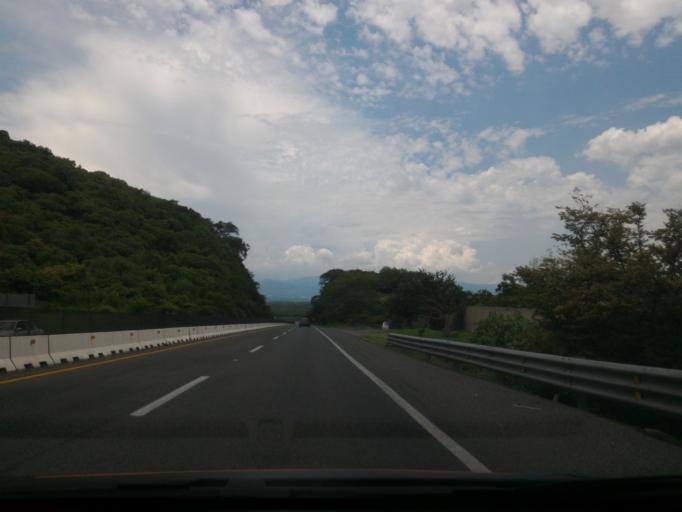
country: MX
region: Jalisco
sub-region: Acatlan de Juarez
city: Villa de los Ninos
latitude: 20.3912
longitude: -103.5727
